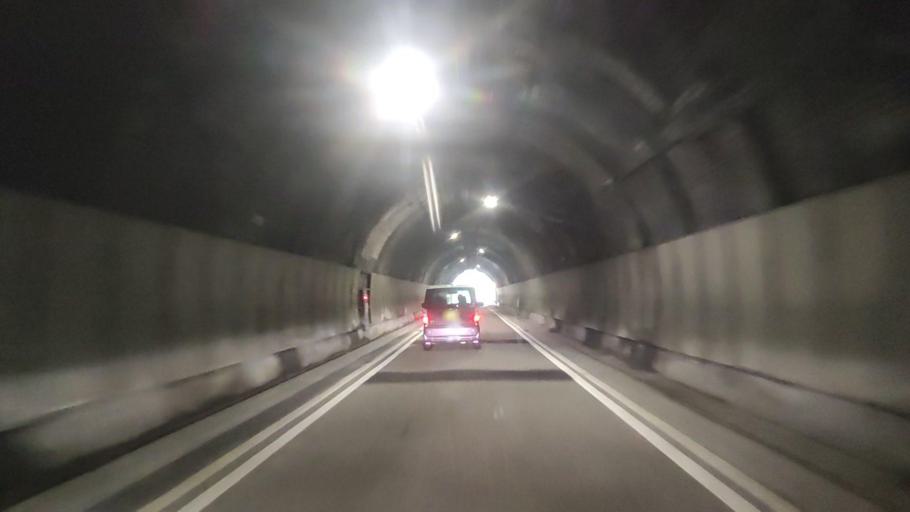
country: JP
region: Fukui
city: Takefu
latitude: 35.8467
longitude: 136.1250
